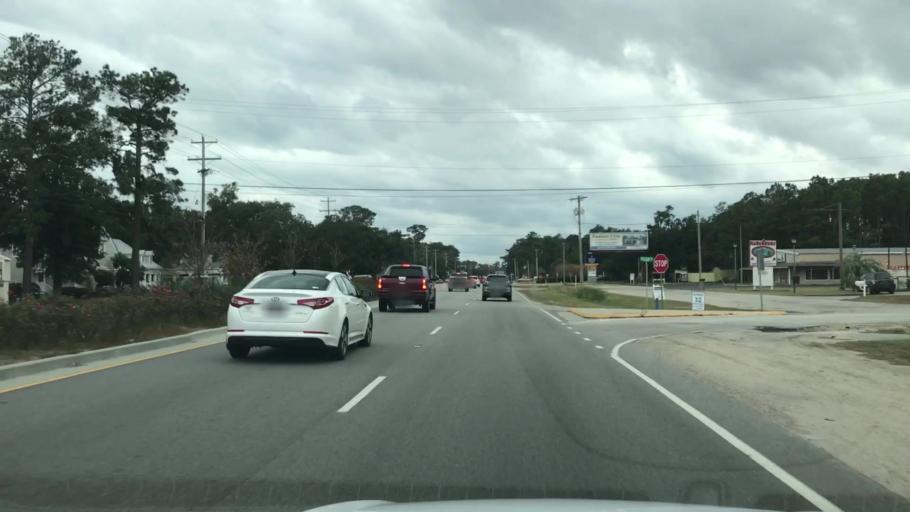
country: US
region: South Carolina
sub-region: Georgetown County
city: Murrells Inlet
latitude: 33.4475
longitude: -79.1211
